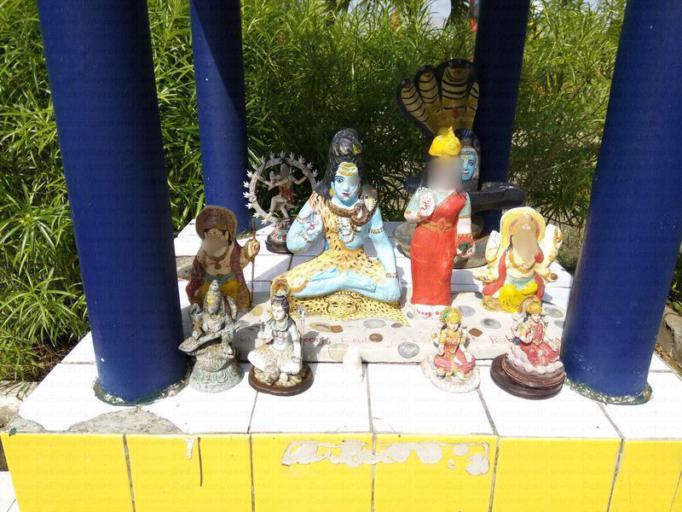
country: SR
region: Paramaribo
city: Paramaribo
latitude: 5.9035
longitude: -55.2259
